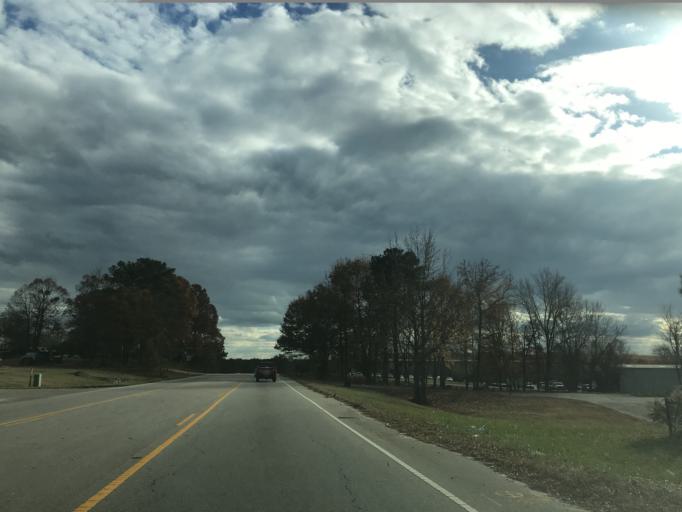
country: US
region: North Carolina
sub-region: Wake County
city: Raleigh
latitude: 35.7949
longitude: -78.5625
